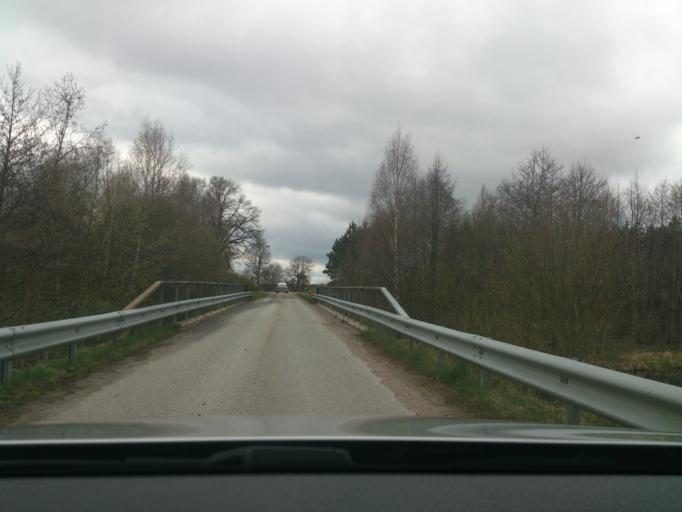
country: SE
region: Vaestra Goetaland
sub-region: Ulricehamns Kommun
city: Ulricehamn
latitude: 57.9559
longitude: 13.5245
